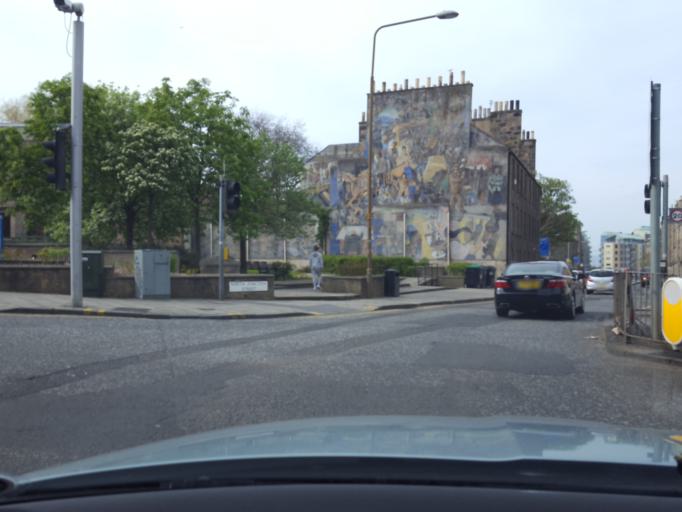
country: GB
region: Scotland
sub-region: Edinburgh
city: Edinburgh
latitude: 55.9755
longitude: -3.1792
